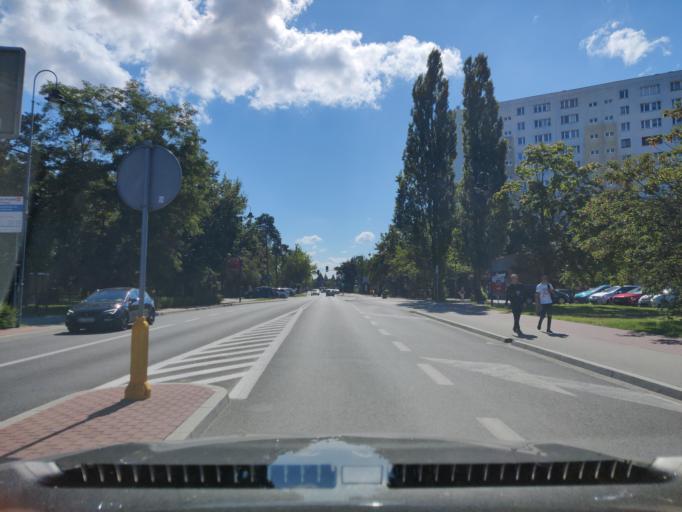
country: PL
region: Masovian Voivodeship
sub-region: Powiat legionowski
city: Legionowo
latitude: 52.3948
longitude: 20.9305
